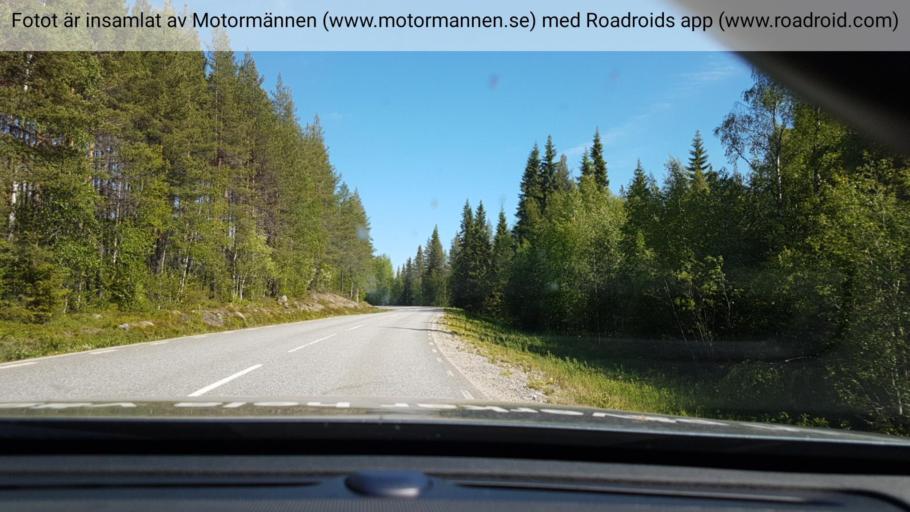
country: SE
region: Vaesterbotten
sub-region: Lycksele Kommun
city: Soderfors
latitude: 64.6213
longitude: 18.2717
